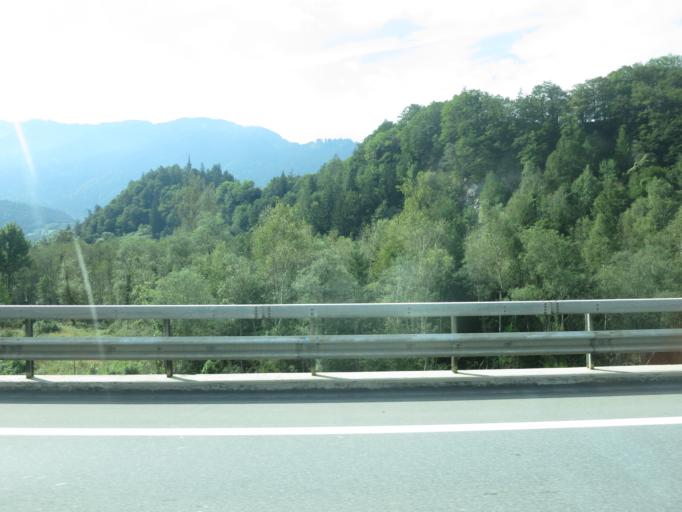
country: CH
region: Grisons
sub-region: Imboden District
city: Bonaduz
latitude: 46.8066
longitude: 9.4137
